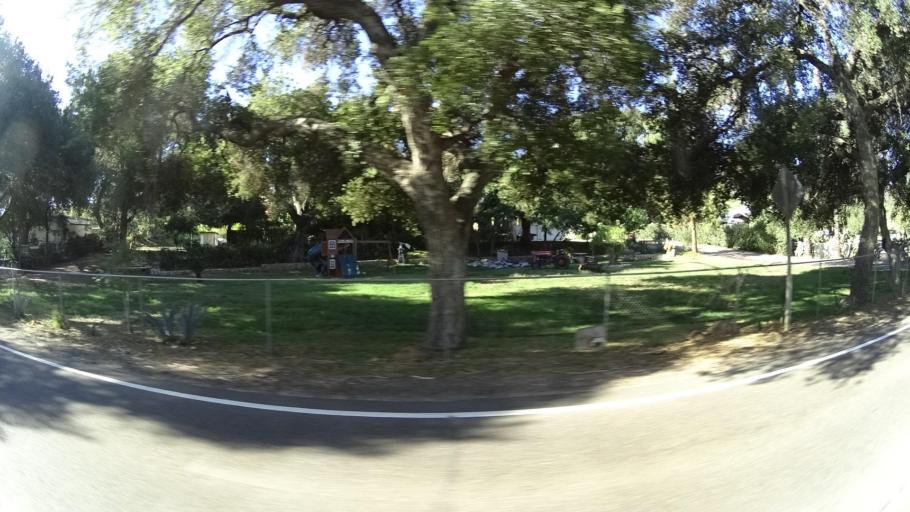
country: US
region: California
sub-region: San Diego County
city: Jamul
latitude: 32.6446
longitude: -116.7820
